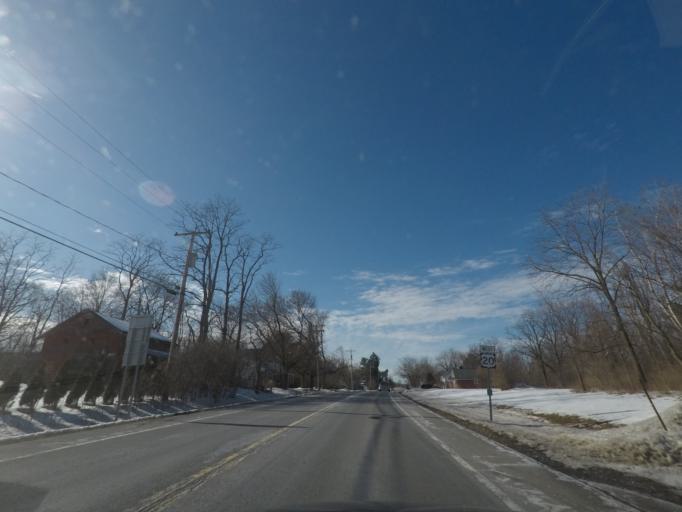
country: US
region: New York
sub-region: Albany County
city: Altamont
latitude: 42.7397
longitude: -74.0147
